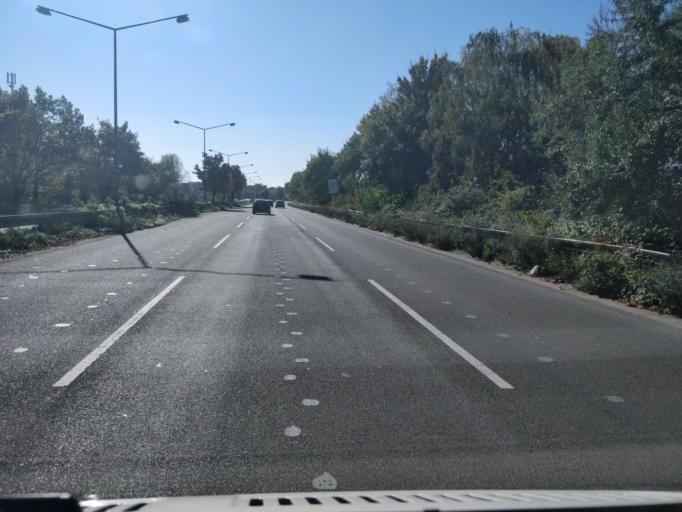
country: DE
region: North Rhine-Westphalia
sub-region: Regierungsbezirk Koln
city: Bilderstoeckchen
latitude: 51.0018
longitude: 6.9471
